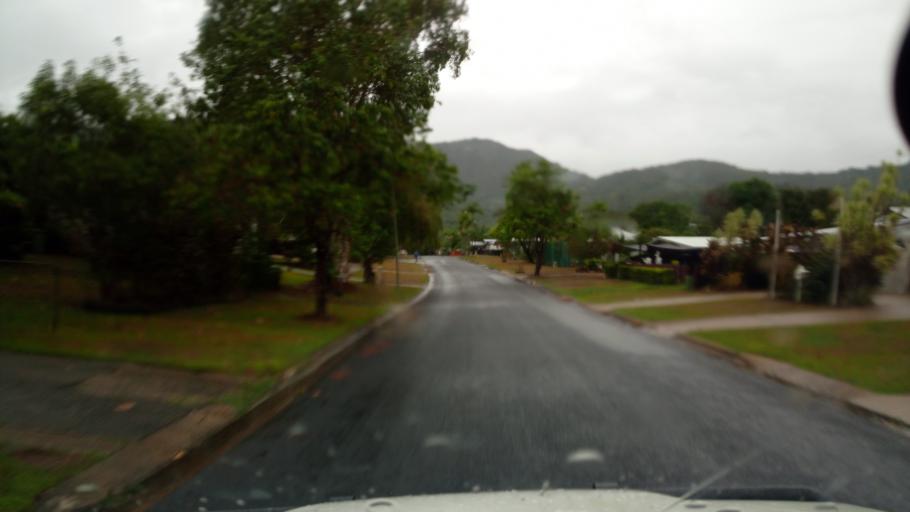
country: AU
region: Queensland
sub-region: Cairns
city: Woree
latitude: -16.9557
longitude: 145.7343
